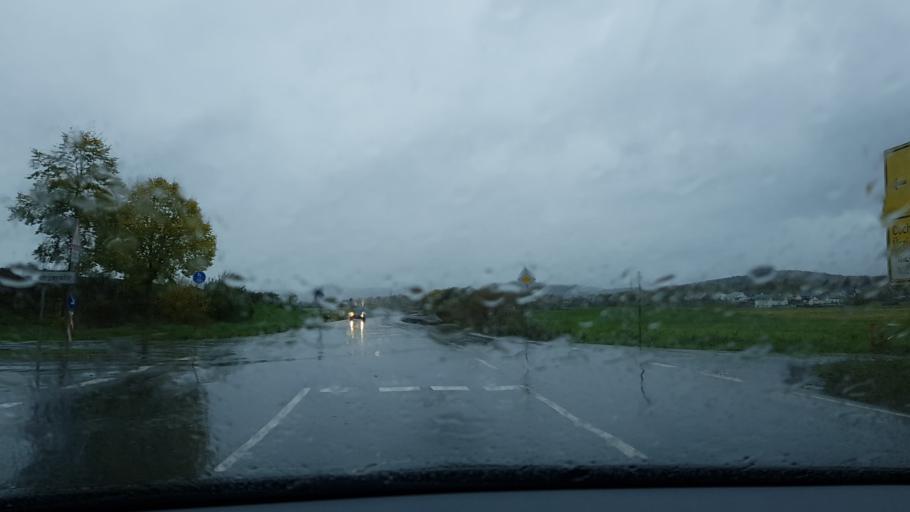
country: DE
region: Rheinland-Pfalz
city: Neuerburg
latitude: 49.9917
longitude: 6.9388
